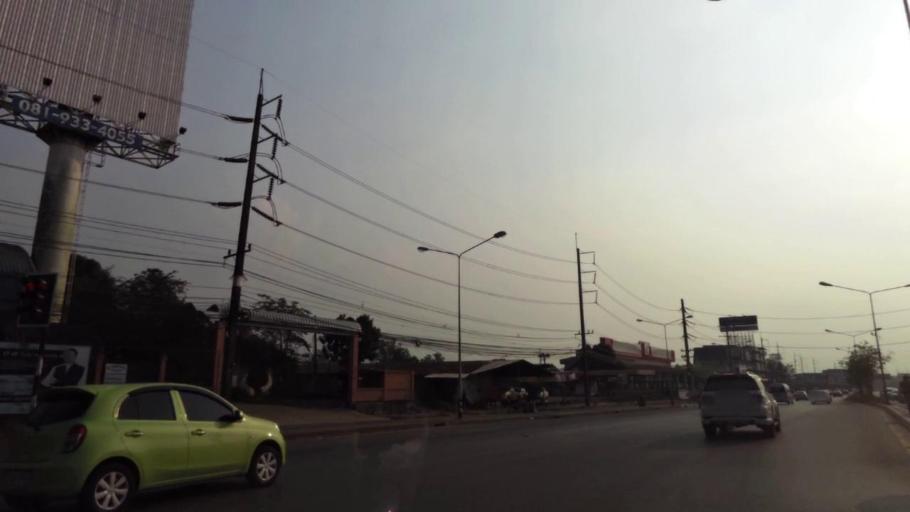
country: TH
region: Chanthaburi
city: Chanthaburi
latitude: 12.6240
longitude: 102.1517
